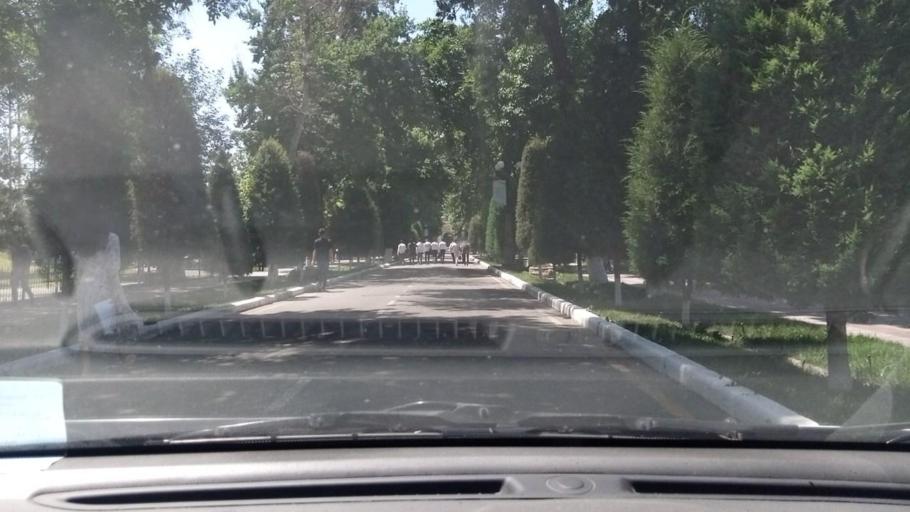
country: UZ
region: Toshkent Shahri
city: Tashkent
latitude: 41.2757
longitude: 69.2804
